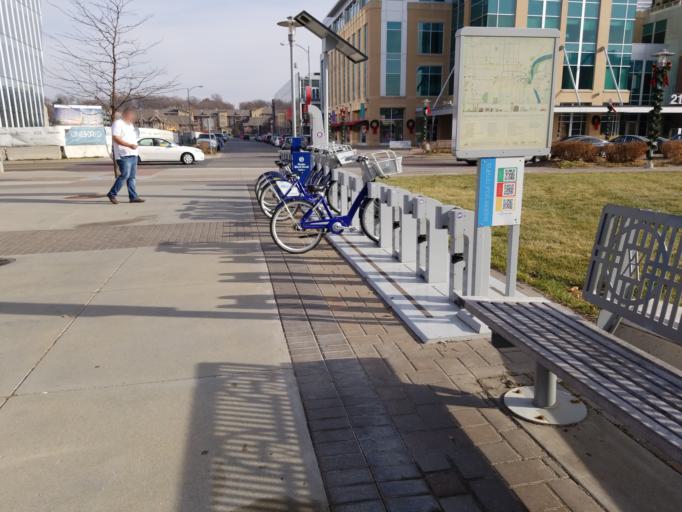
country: US
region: Nebraska
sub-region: Douglas County
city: Ralston
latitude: 41.2399
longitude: -96.0151
